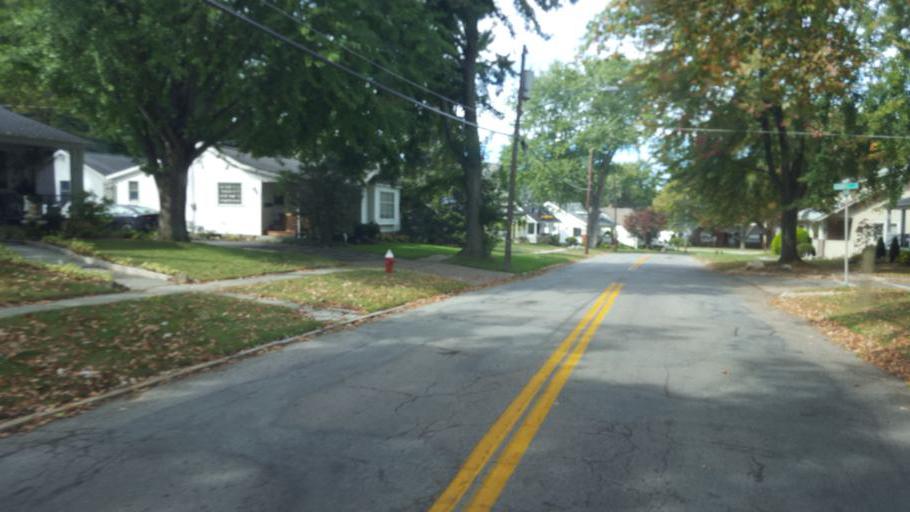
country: US
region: Ohio
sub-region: Lorain County
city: Amherst
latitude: 41.4007
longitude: -82.2256
